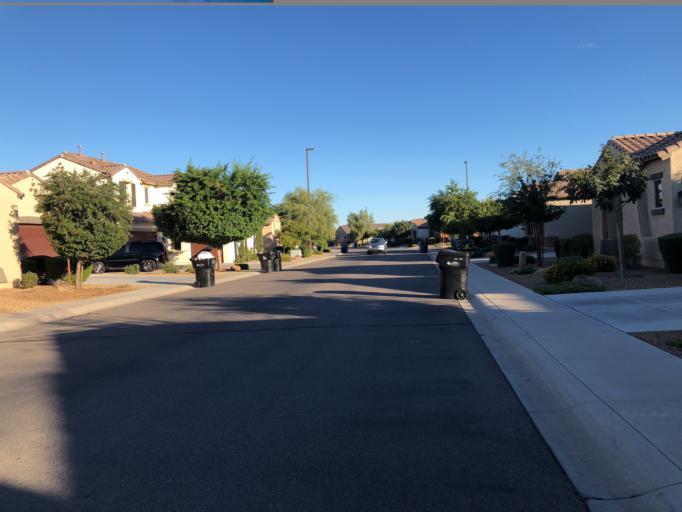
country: US
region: Arizona
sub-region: Maricopa County
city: Queen Creek
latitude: 33.2263
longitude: -111.7086
